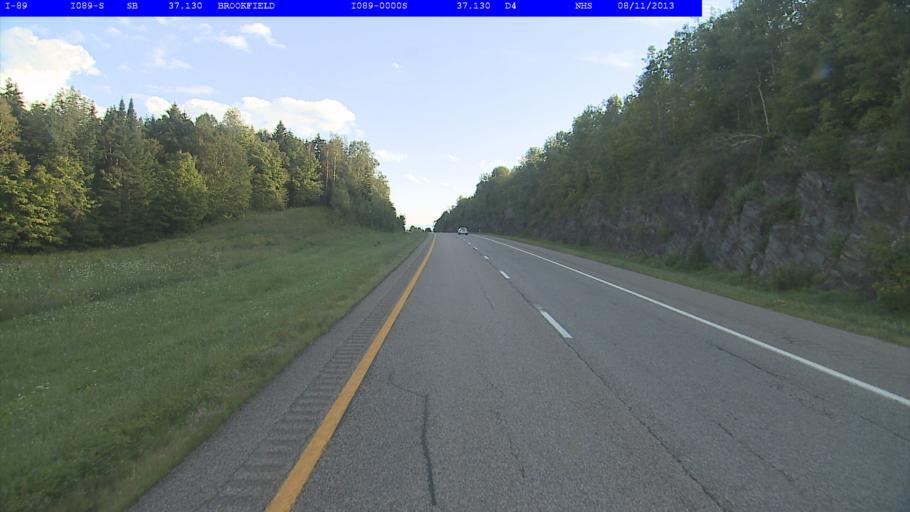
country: US
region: Vermont
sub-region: Orange County
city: Williamstown
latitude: 44.0342
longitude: -72.6153
